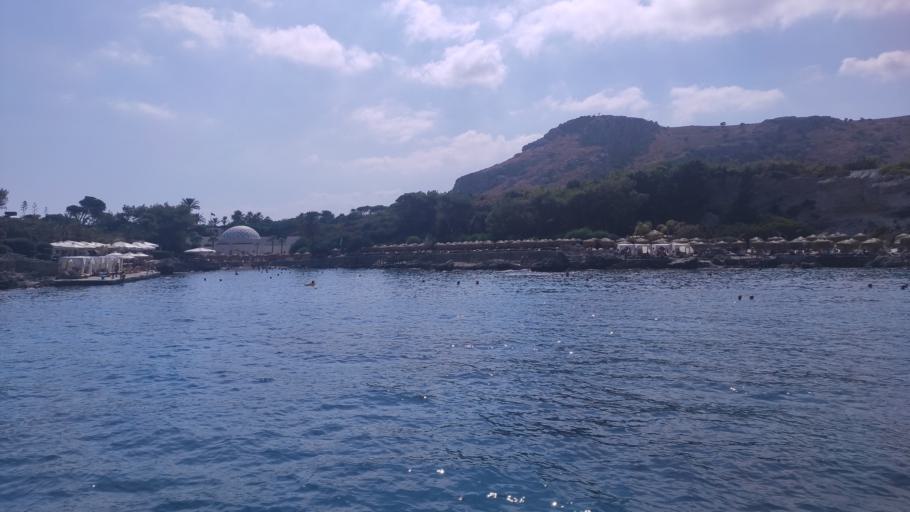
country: GR
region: South Aegean
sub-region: Nomos Dodekanisou
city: Faliraki
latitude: 36.3793
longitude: 28.2397
